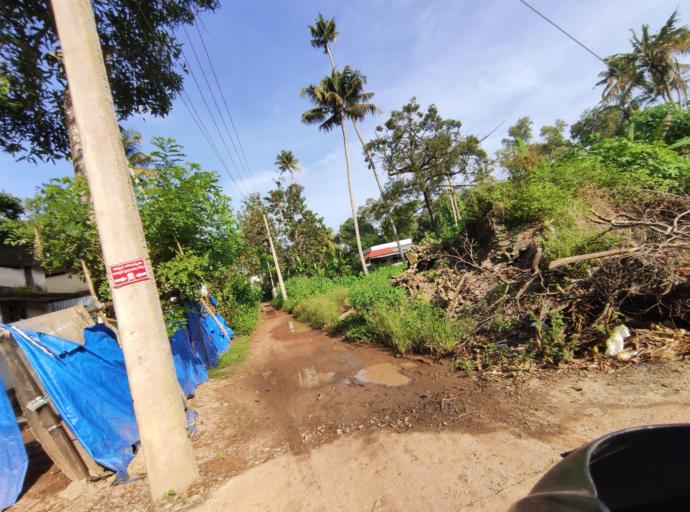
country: IN
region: Kerala
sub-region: Alappuzha
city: Vayalar
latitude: 9.6889
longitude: 76.3386
